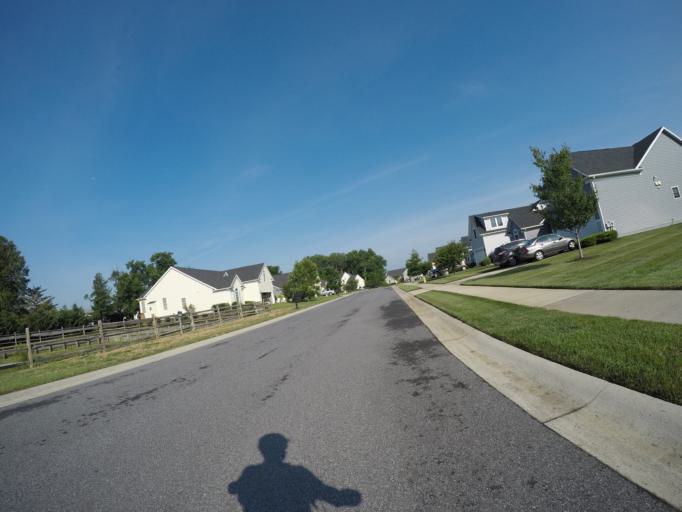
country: US
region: Delaware
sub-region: Sussex County
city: Ocean View
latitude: 38.5628
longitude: -75.0758
